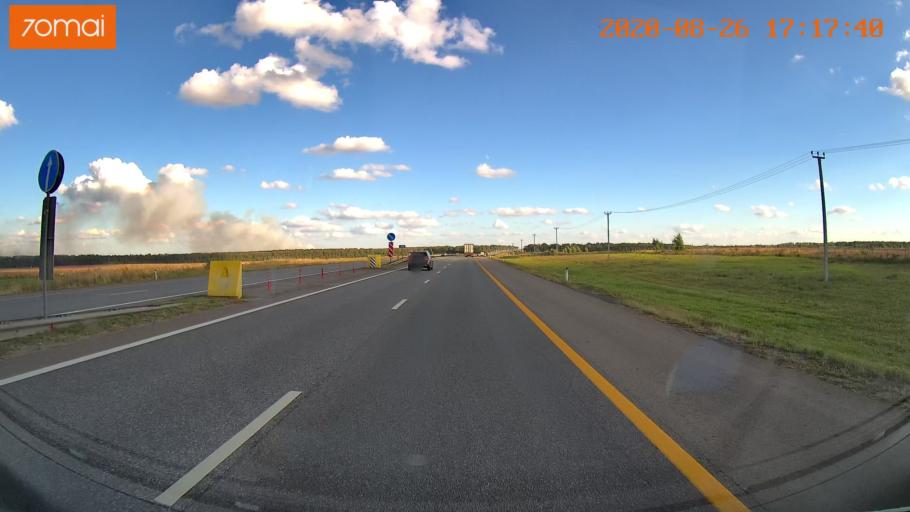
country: RU
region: Tula
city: Volovo
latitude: 53.6220
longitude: 38.0885
